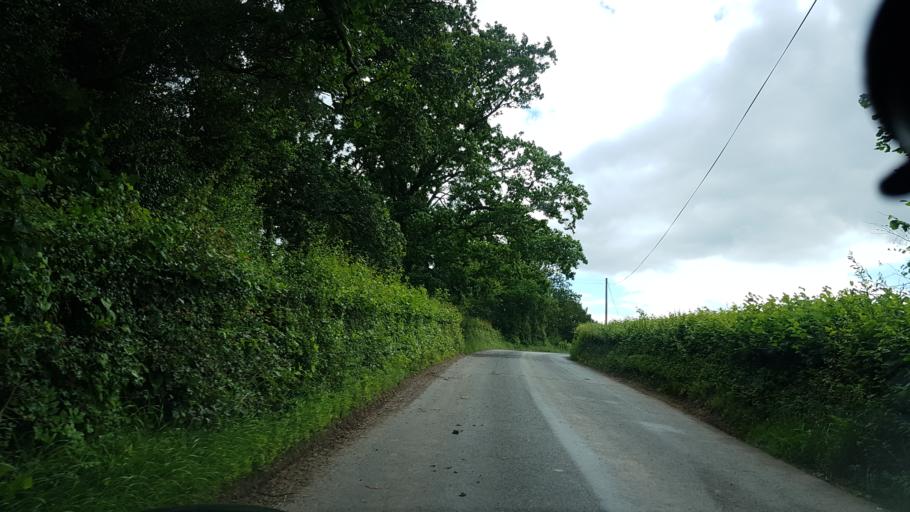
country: GB
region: England
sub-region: Herefordshire
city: Llancillo
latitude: 51.8862
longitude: -2.9511
